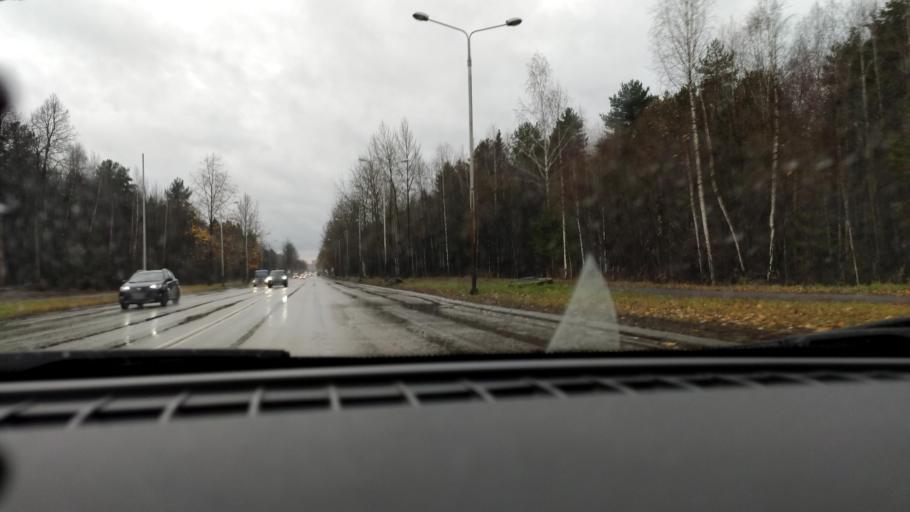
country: RU
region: Perm
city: Perm
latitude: 58.0889
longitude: 56.3808
